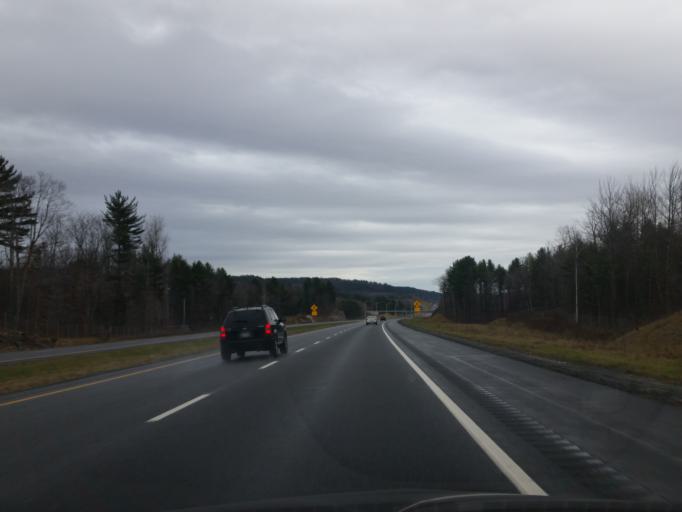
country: CA
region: Quebec
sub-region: Outaouais
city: Papineauville
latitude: 45.6731
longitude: -74.9283
